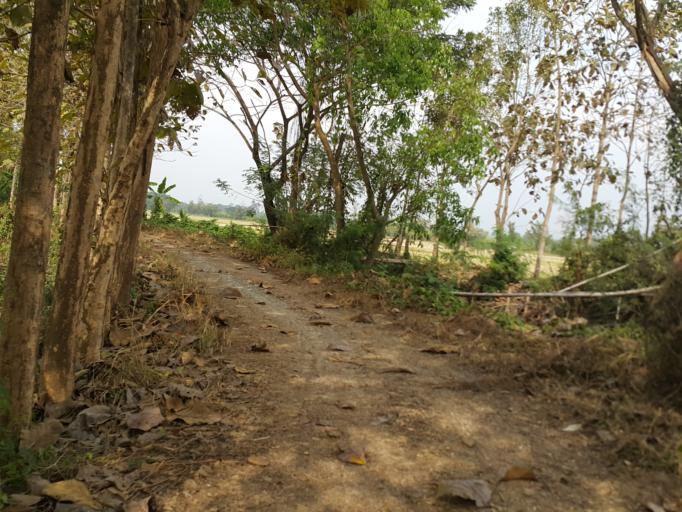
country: TH
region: Chiang Mai
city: San Kamphaeng
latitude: 18.7860
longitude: 99.1144
